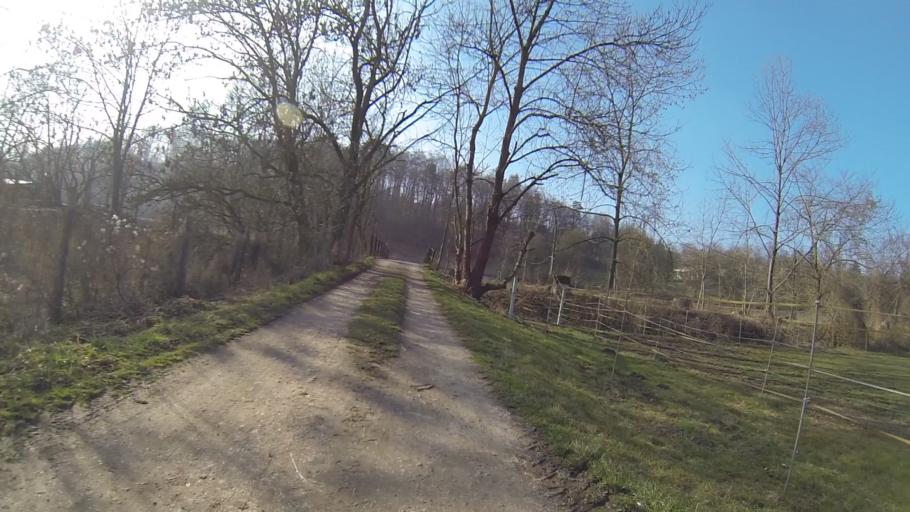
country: DE
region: Baden-Wuerttemberg
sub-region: Regierungsbezirk Stuttgart
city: Bolheim
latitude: 48.6421
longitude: 10.1566
